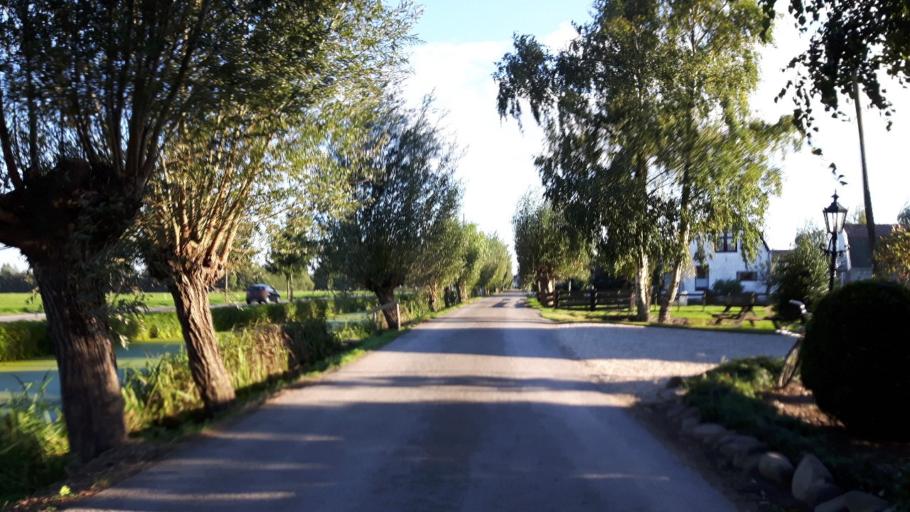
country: NL
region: Utrecht
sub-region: Gemeente Oudewater
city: Oudewater
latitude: 52.0389
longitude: 4.8575
